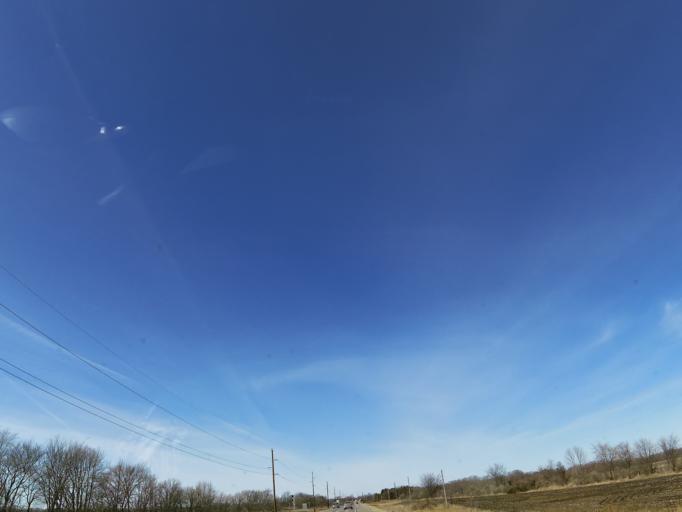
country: US
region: Minnesota
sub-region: Wright County
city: Annandale
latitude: 45.2706
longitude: -94.1630
